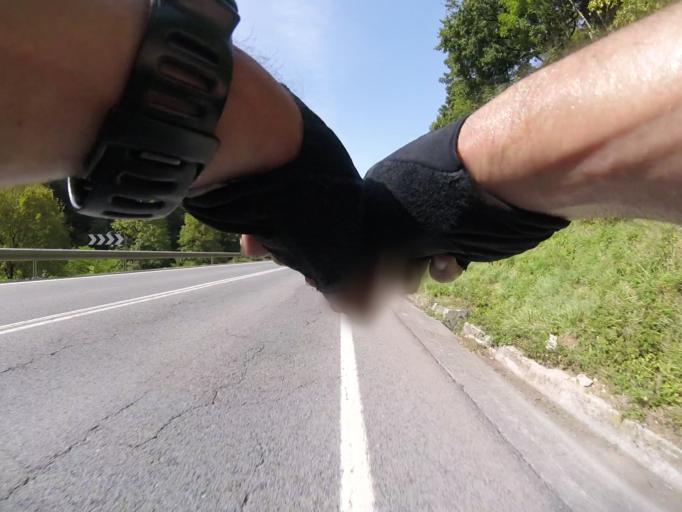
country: ES
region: Navarre
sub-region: Provincia de Navarra
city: Doneztebe
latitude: 43.1419
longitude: -1.5881
